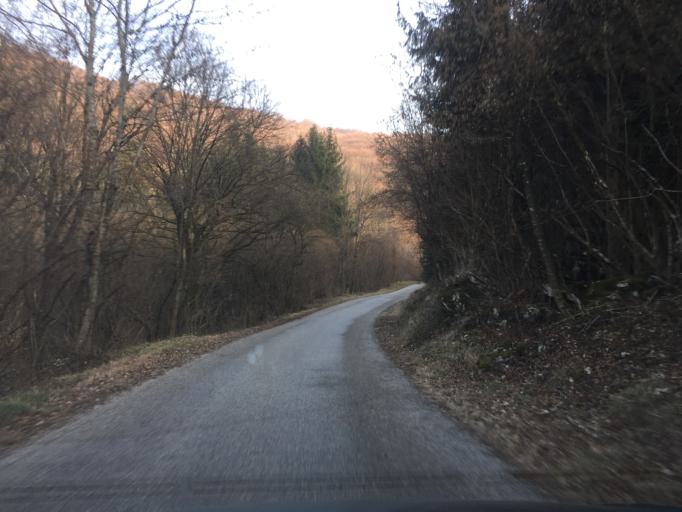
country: SI
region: Kanal
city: Kanal
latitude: 46.0614
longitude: 13.6662
